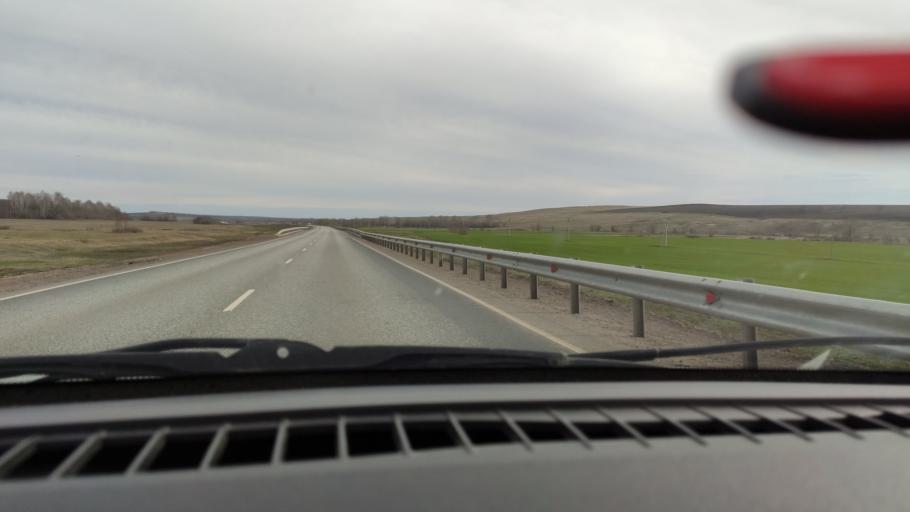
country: RU
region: Bashkortostan
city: Yermolayevo
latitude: 52.6243
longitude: 55.8434
